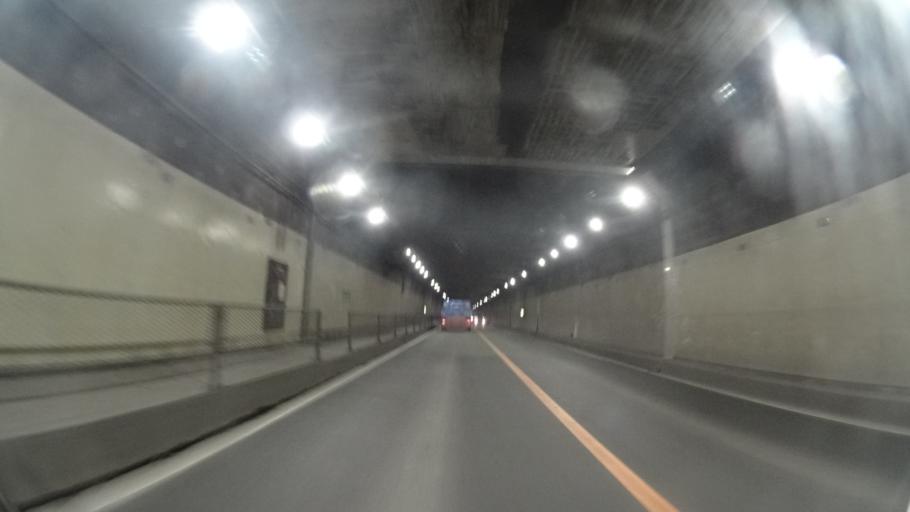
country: JP
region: Kumamoto
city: Ozu
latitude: 32.8353
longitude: 130.8549
